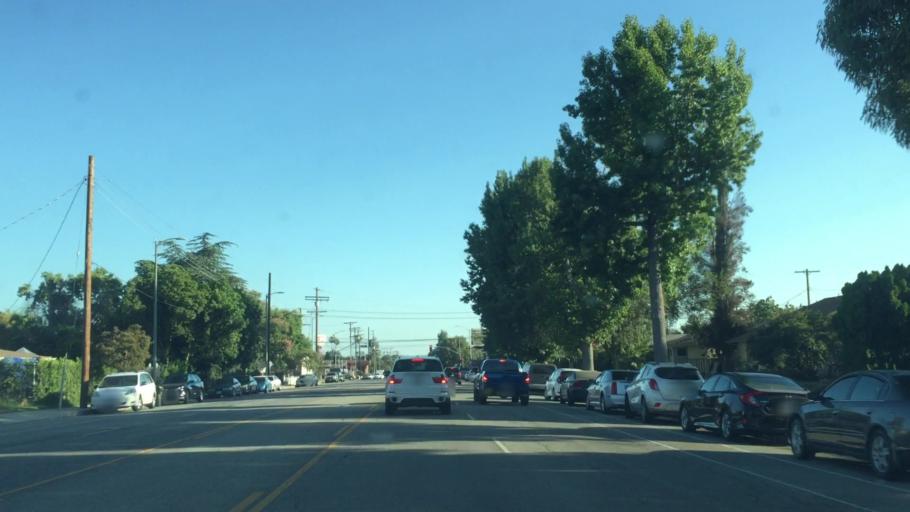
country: US
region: California
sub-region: Los Angeles County
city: Northridge
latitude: 34.2373
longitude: -118.4851
